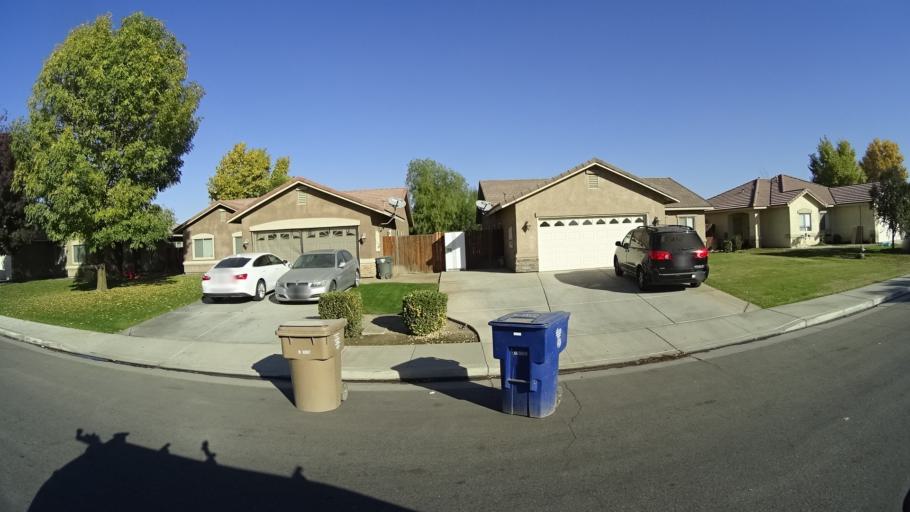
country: US
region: California
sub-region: Kern County
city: Greenfield
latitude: 35.2691
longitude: -119.0423
